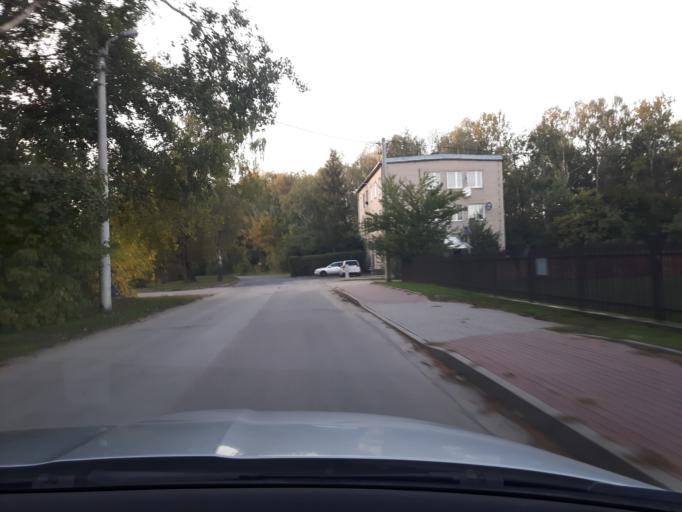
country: PL
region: Masovian Voivodeship
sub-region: Powiat wolominski
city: Kobylka
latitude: 52.3455
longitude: 21.1837
